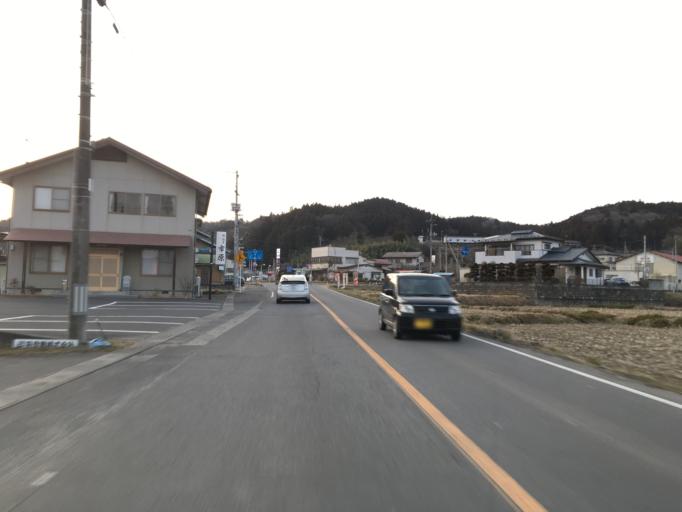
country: JP
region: Fukushima
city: Ishikawa
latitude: 37.0291
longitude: 140.3761
